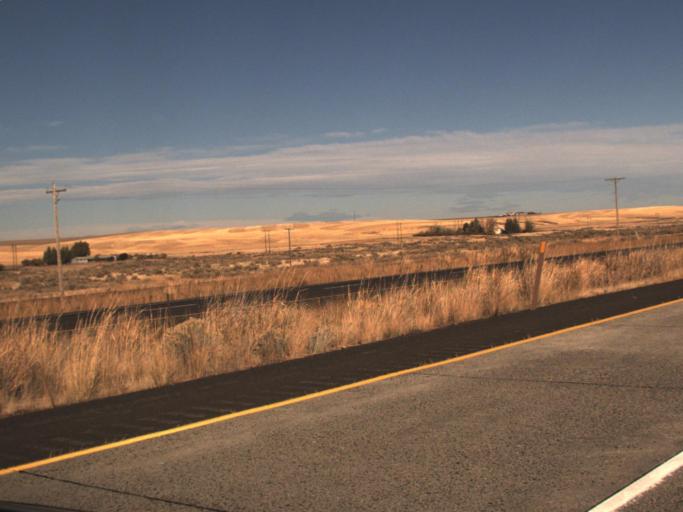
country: US
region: Washington
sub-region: Adams County
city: Ritzville
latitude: 47.0795
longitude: -118.4106
